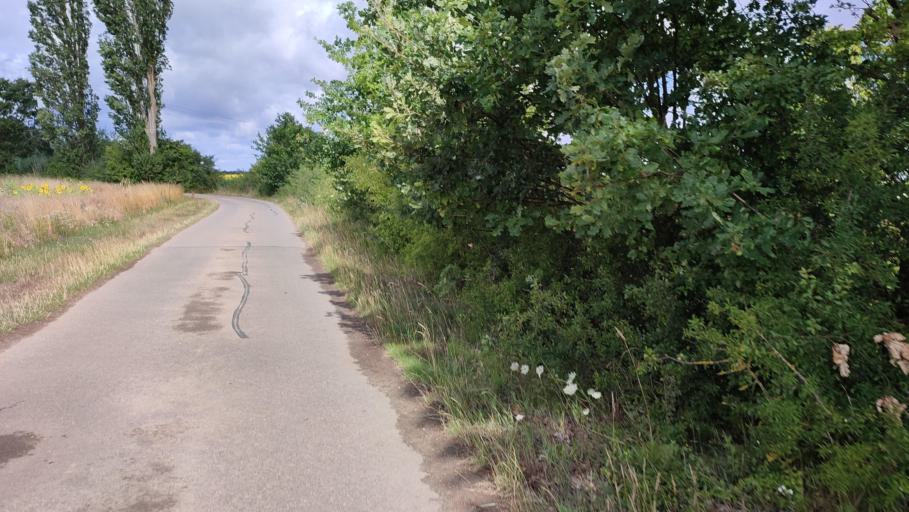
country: DE
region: Lower Saxony
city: Neu Darchau
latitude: 53.2334
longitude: 10.9671
